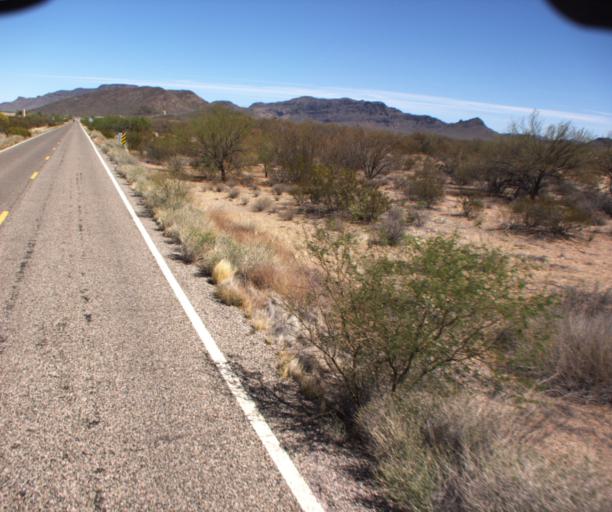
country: US
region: Arizona
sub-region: Pima County
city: Ajo
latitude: 32.2515
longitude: -112.7452
